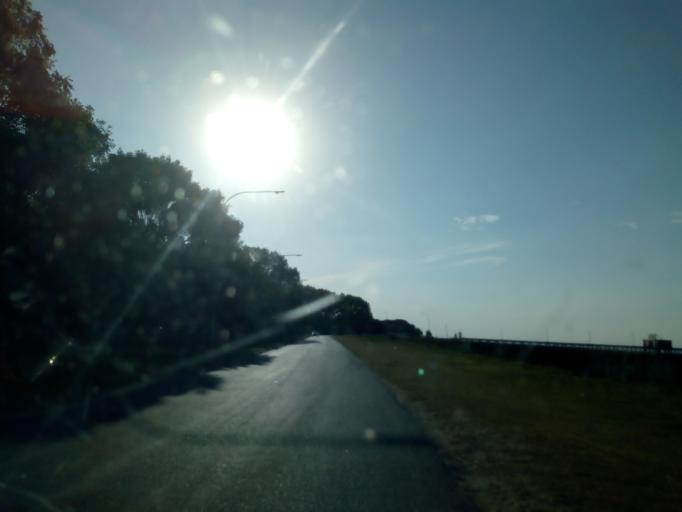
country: AR
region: Buenos Aires
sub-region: Partido de Ensenada
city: Ensenada
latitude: -34.7839
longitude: -58.0075
